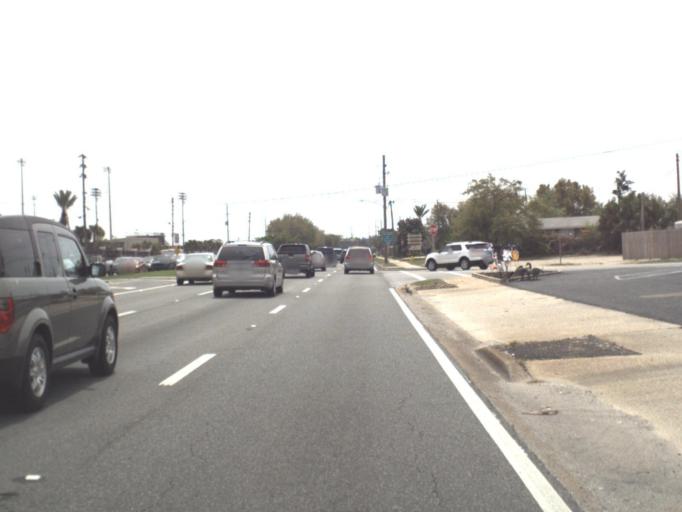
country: US
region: Florida
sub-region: Santa Rosa County
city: Gulf Breeze
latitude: 30.3649
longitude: -87.1700
